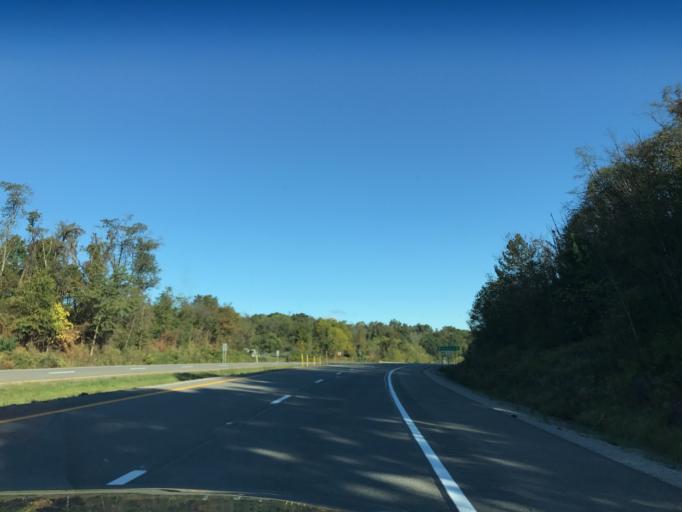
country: US
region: West Virginia
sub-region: Wood County
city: Mineral Wells
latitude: 39.2528
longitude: -81.4836
